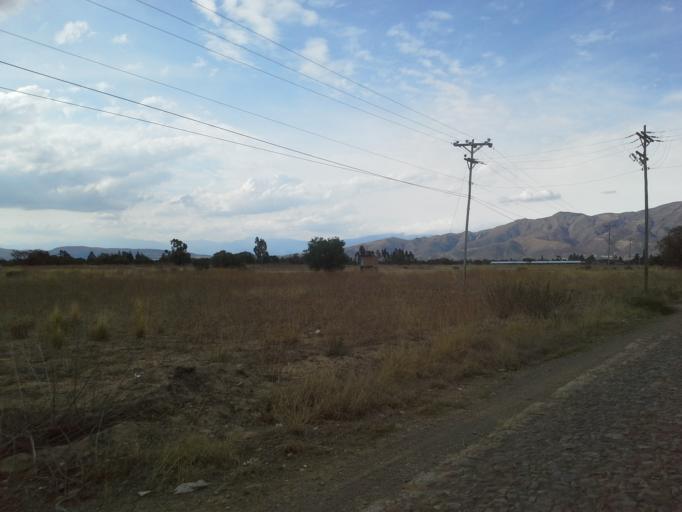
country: BO
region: Cochabamba
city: Tarata
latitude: -17.5975
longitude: -66.0186
